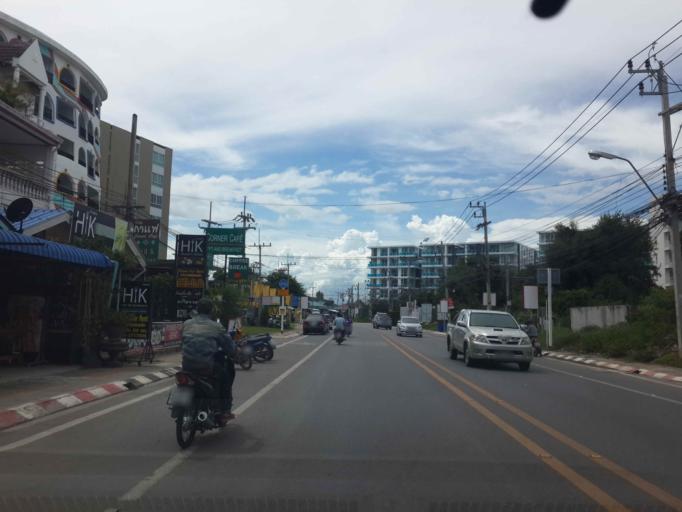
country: TH
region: Prachuap Khiri Khan
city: Hua Hin
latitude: 12.5286
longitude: 99.9690
